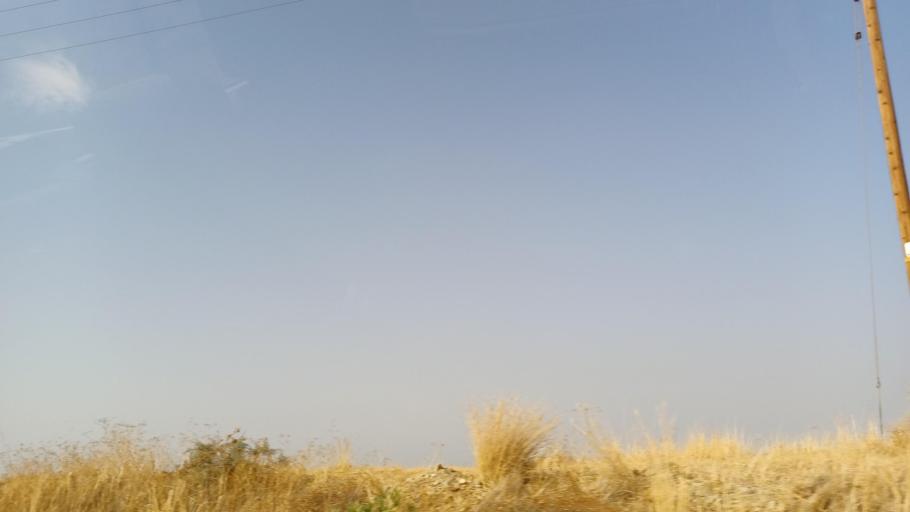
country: CY
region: Lefkosia
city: Astromeritis
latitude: 35.1136
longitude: 32.9915
